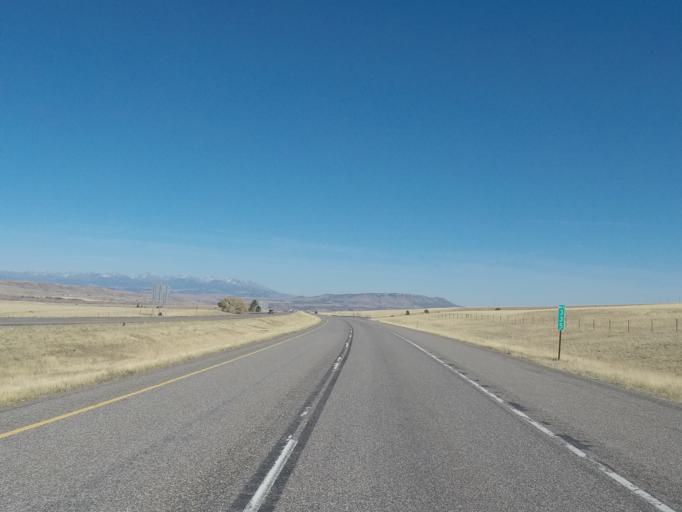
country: US
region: Montana
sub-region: Park County
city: Livingston
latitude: 45.6554
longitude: -110.5375
